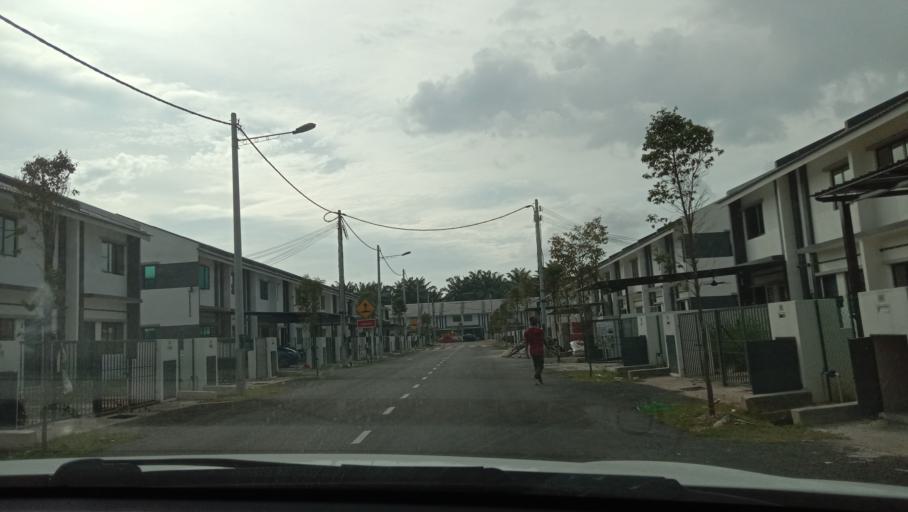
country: MY
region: Selangor
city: Ladang Seri Kundang
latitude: 3.2349
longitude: 101.4786
